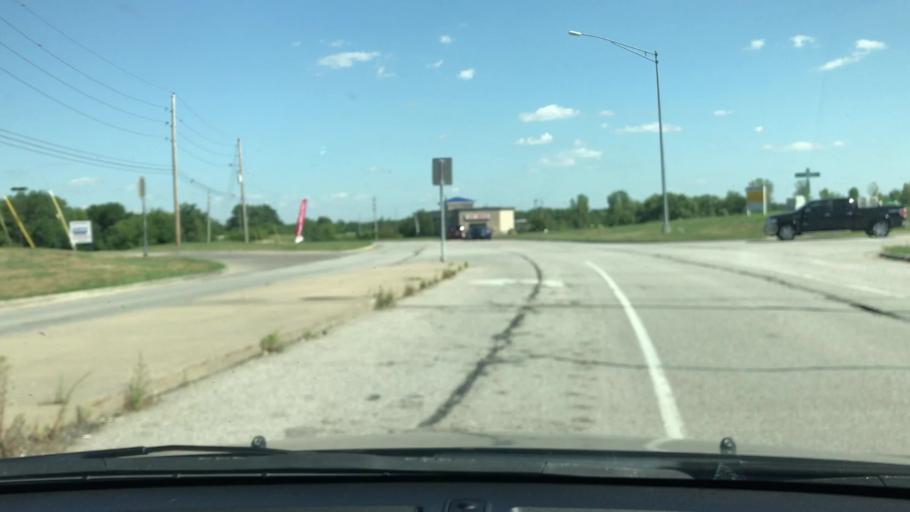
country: US
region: Missouri
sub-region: Cass County
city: Lake Winnebago
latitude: 38.8511
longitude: -94.3791
